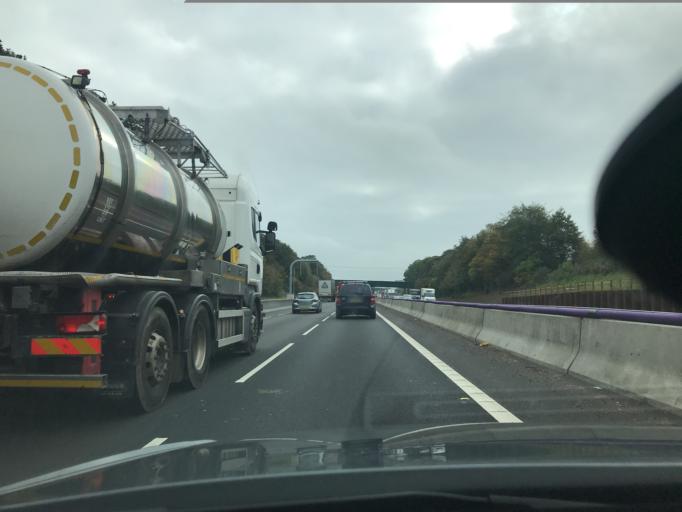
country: GB
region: England
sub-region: Cheshire East
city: Holmes Chapel
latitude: 53.1837
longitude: -2.3709
